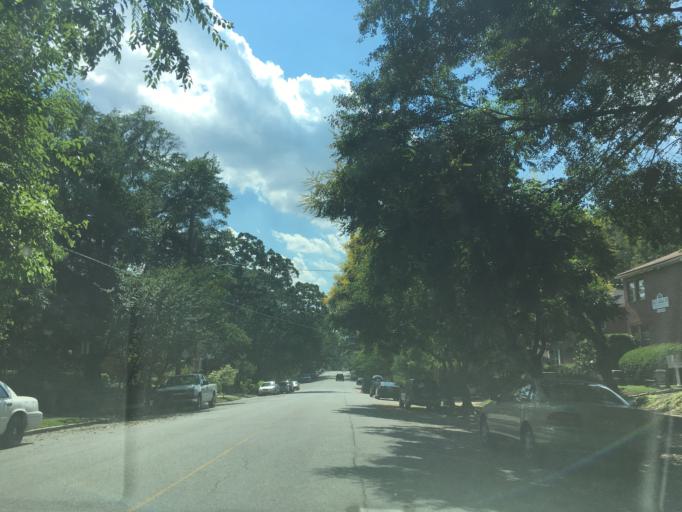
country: US
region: Georgia
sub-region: DeKalb County
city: Druid Hills
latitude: 33.7755
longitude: -84.3561
